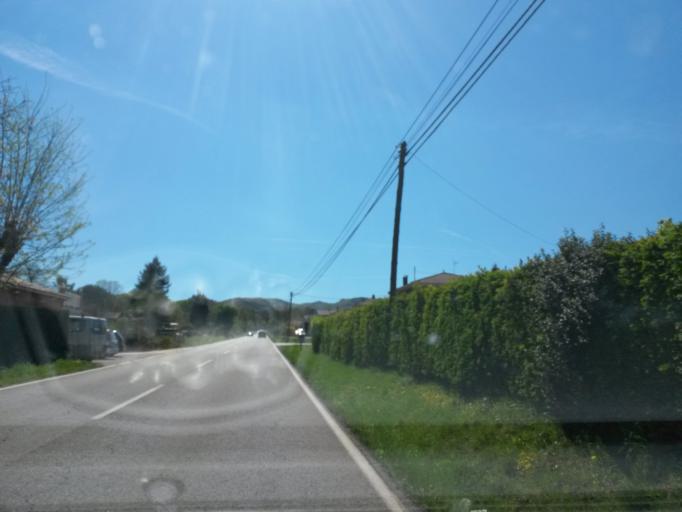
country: ES
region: Catalonia
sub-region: Provincia de Girona
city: Sant Cristofol de les Fonts
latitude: 42.1612
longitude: 2.5115
